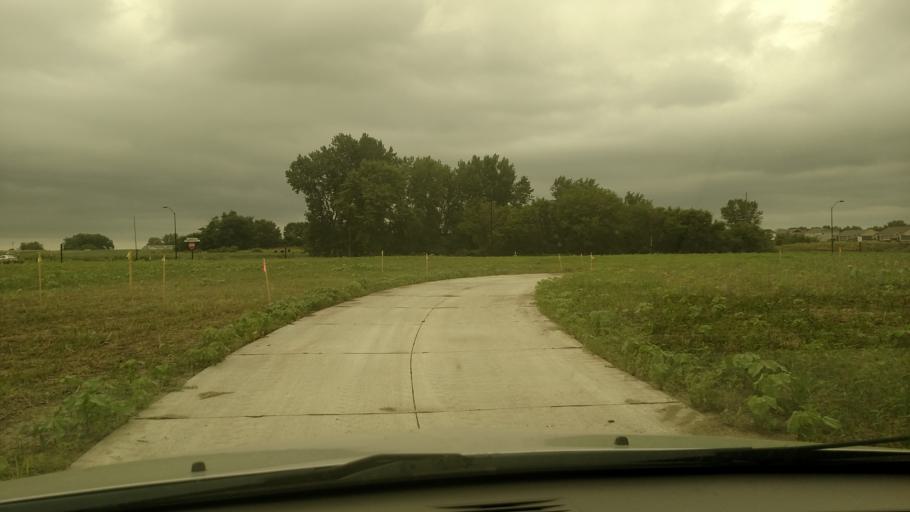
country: US
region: Iowa
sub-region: Polk County
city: Ankeny
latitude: 41.7154
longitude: -93.6127
